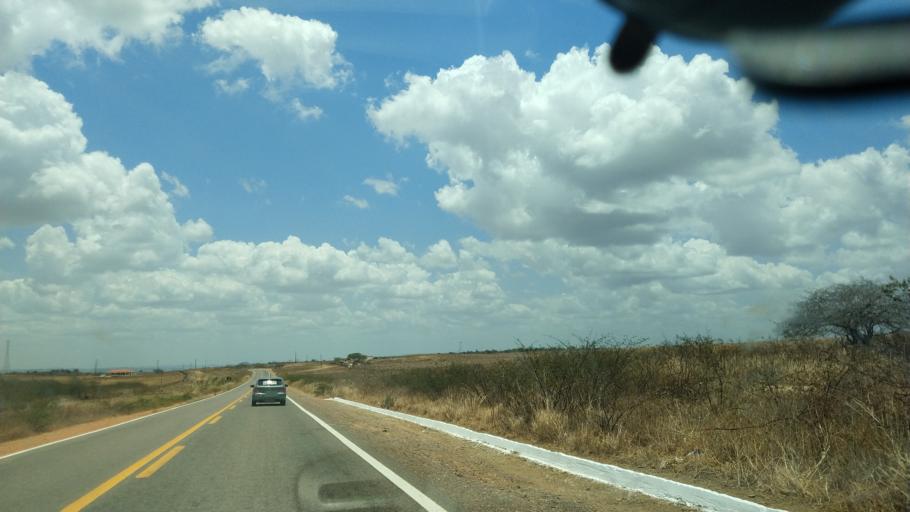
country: BR
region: Rio Grande do Norte
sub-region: Cerro Cora
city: Cerro Cora
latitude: -6.1895
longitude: -36.2509
